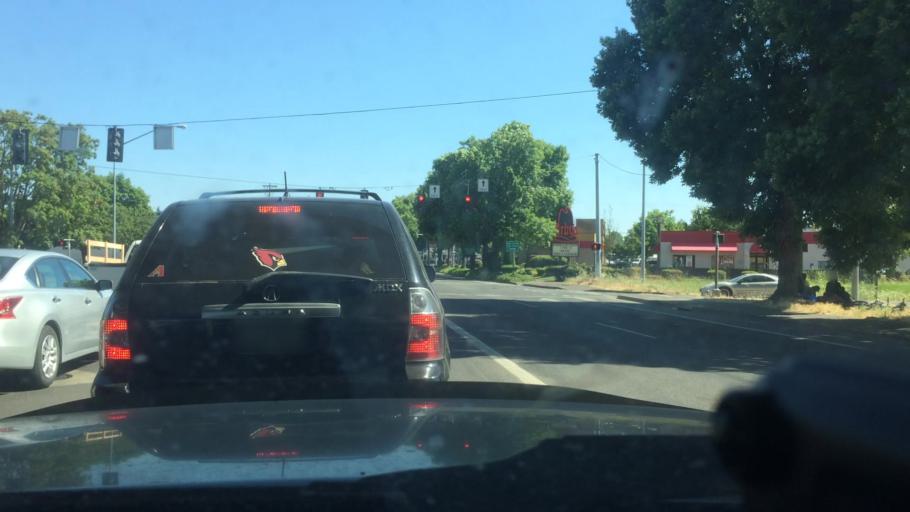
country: US
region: Oregon
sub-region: Lane County
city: Eugene
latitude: 44.0970
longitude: -123.1286
